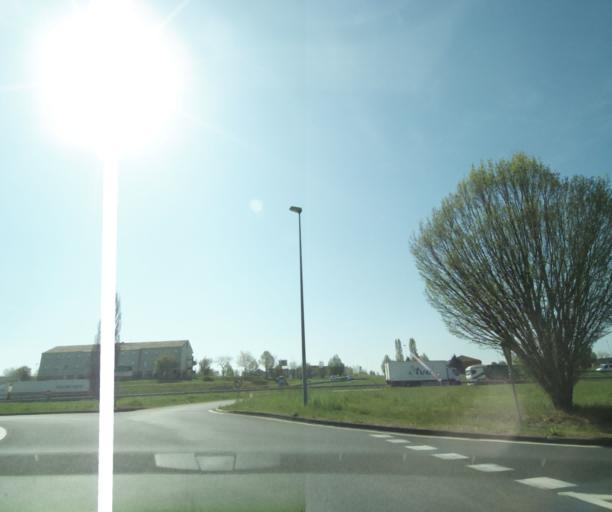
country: FR
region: Bourgogne
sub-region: Departement de Saone-et-Loire
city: Paray-le-Monial
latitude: 46.4698
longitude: 4.1183
